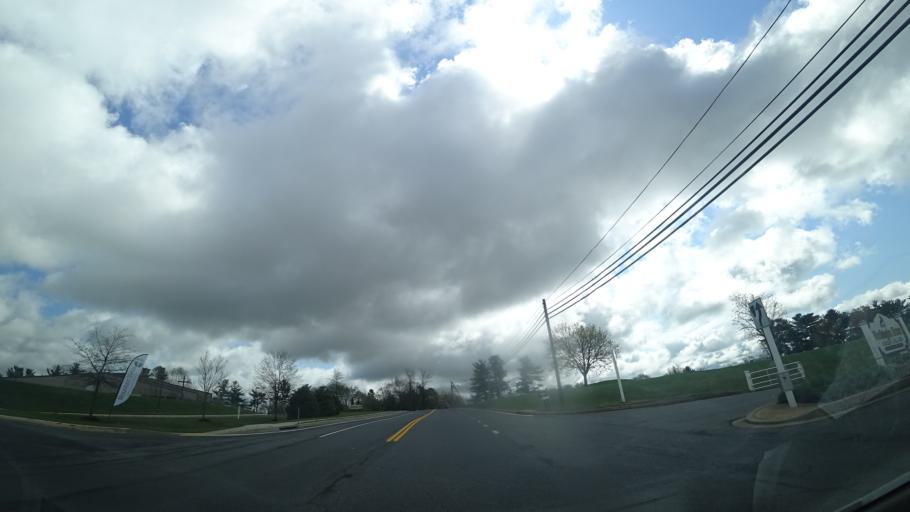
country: US
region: Maryland
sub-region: Frederick County
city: Urbana
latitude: 39.3291
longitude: -77.3749
